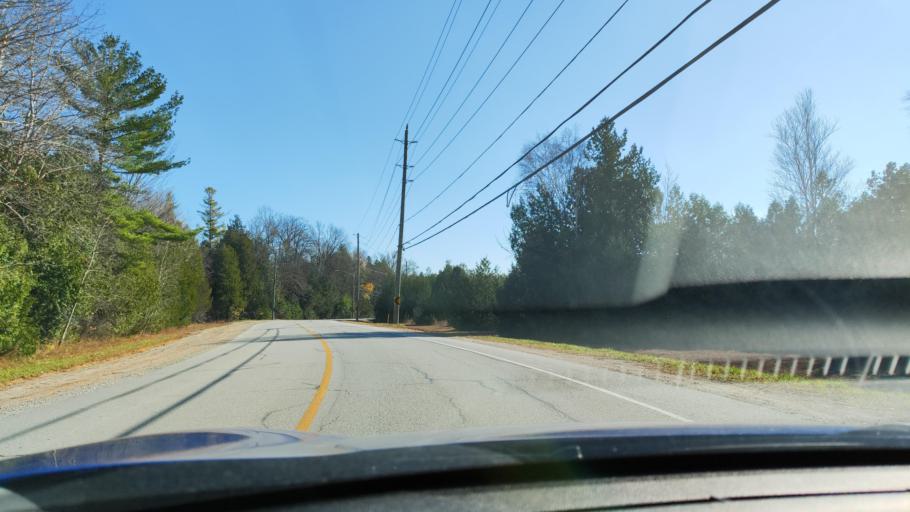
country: CA
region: Ontario
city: Wasaga Beach
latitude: 44.5065
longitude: -79.9939
